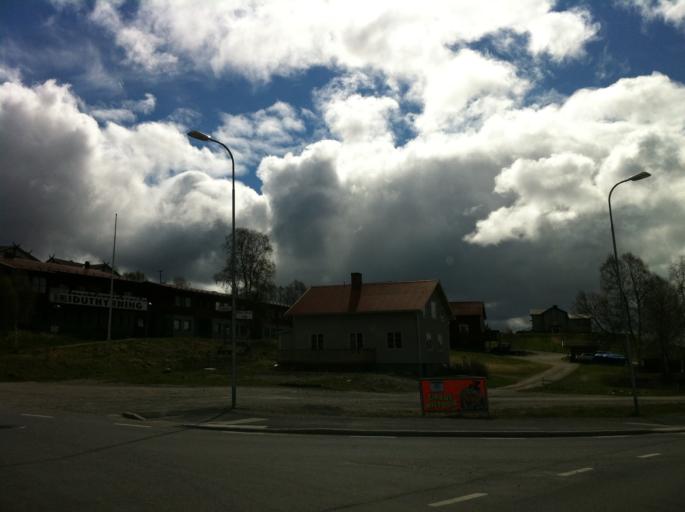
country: NO
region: Hedmark
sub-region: Engerdal
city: Engerdal
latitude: 62.5456
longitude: 12.5443
